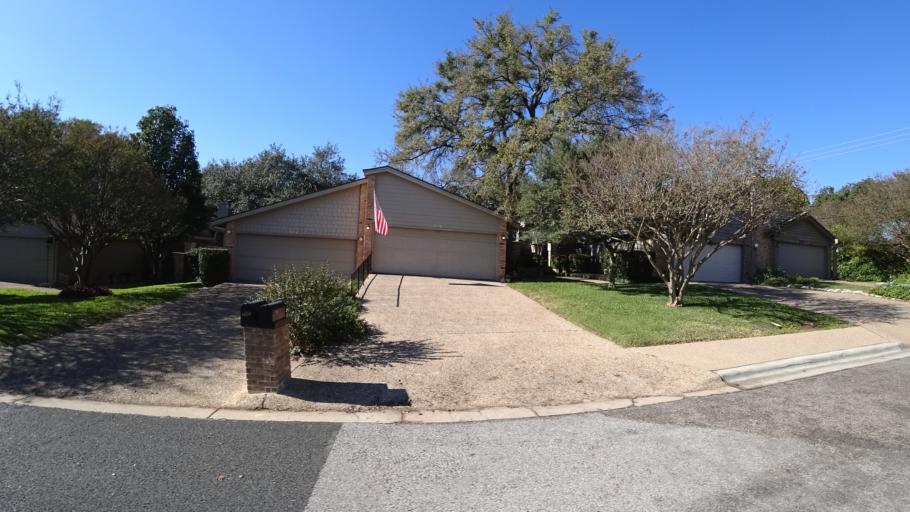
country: US
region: Texas
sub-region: Williamson County
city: Jollyville
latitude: 30.3702
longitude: -97.7475
